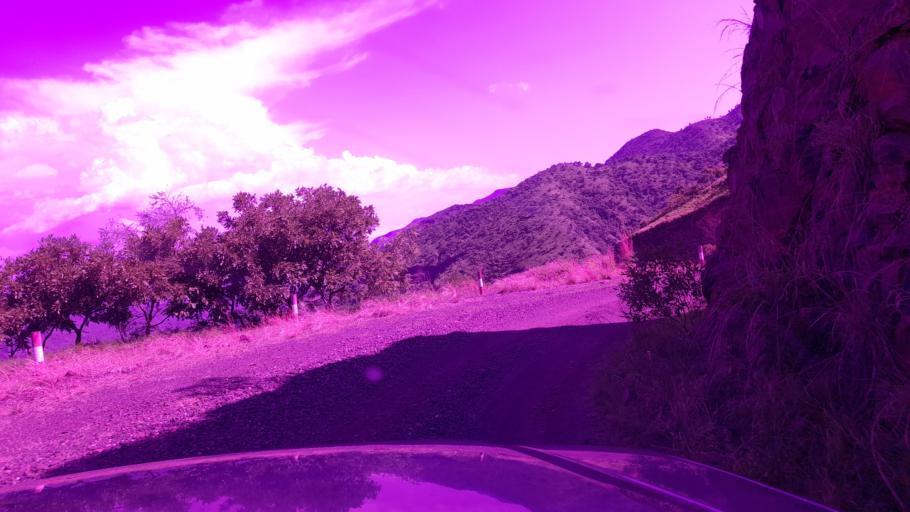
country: ET
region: Southern Nations, Nationalities, and People's Region
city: K'olito
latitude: 7.7789
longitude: 37.5592
